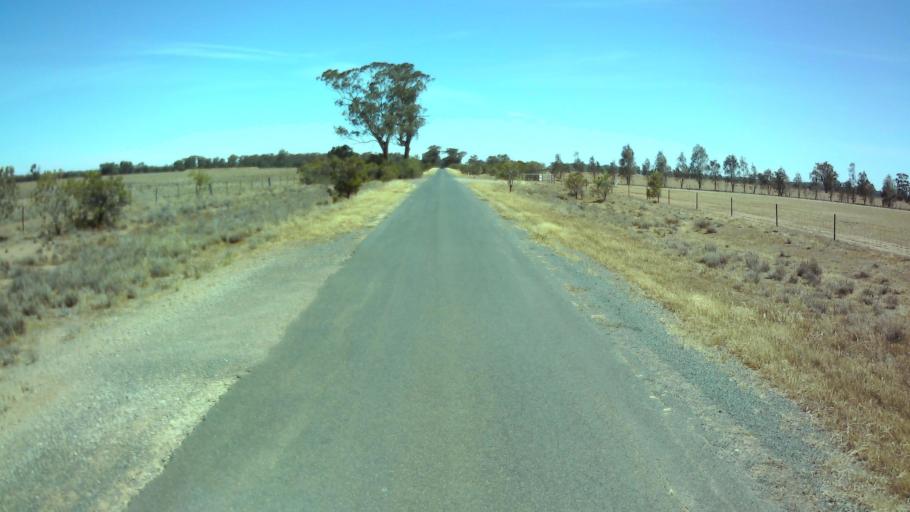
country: AU
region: New South Wales
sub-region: Weddin
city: Grenfell
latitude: -33.8945
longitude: 147.6875
